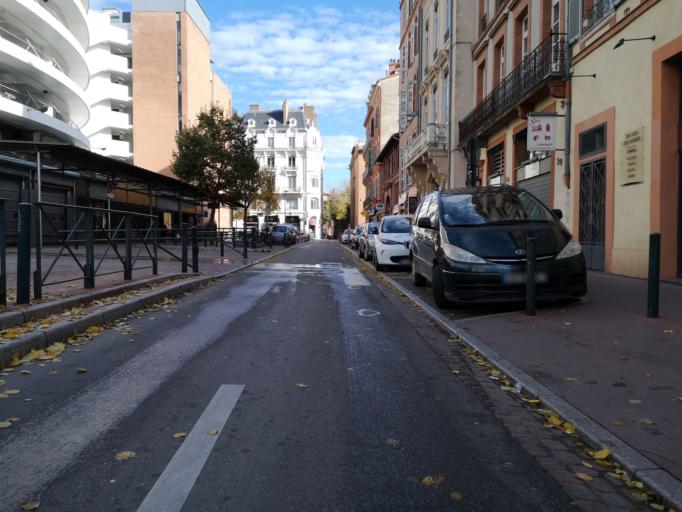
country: FR
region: Midi-Pyrenees
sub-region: Departement de la Haute-Garonne
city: Toulouse
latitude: 43.5973
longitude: 1.4441
